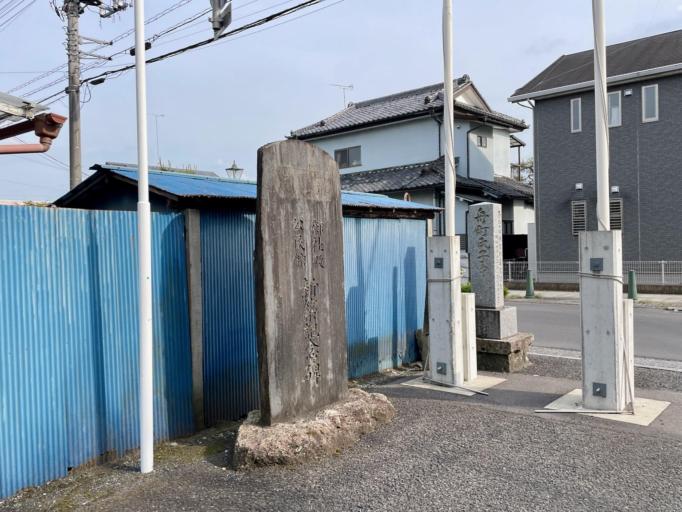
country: JP
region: Tochigi
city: Mibu
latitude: 36.4262
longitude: 139.8048
